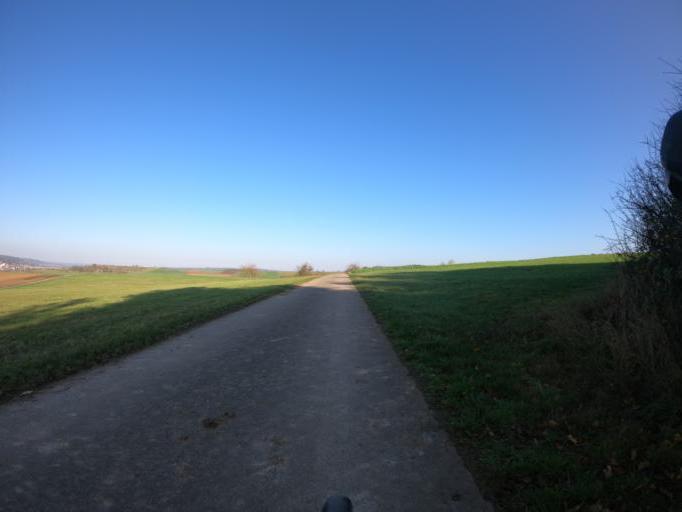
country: DE
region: Baden-Wuerttemberg
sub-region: Regierungsbezirk Stuttgart
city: Weil der Stadt
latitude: 48.7358
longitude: 8.8960
